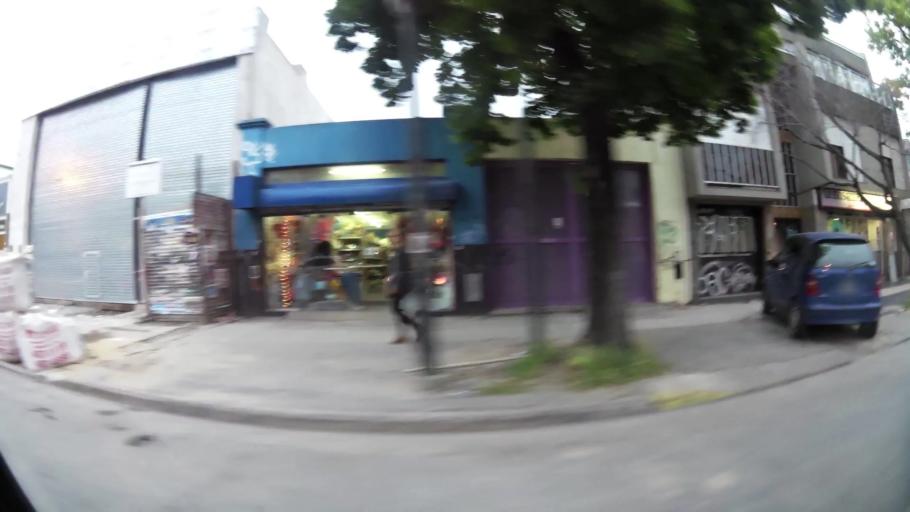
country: AR
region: Buenos Aires
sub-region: Partido de La Plata
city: La Plata
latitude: -34.9093
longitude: -57.9710
